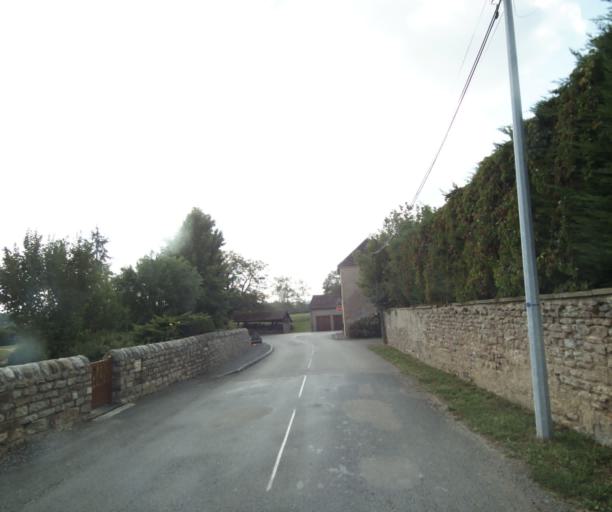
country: FR
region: Bourgogne
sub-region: Departement de Saone-et-Loire
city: Palinges
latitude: 46.4949
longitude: 4.2158
